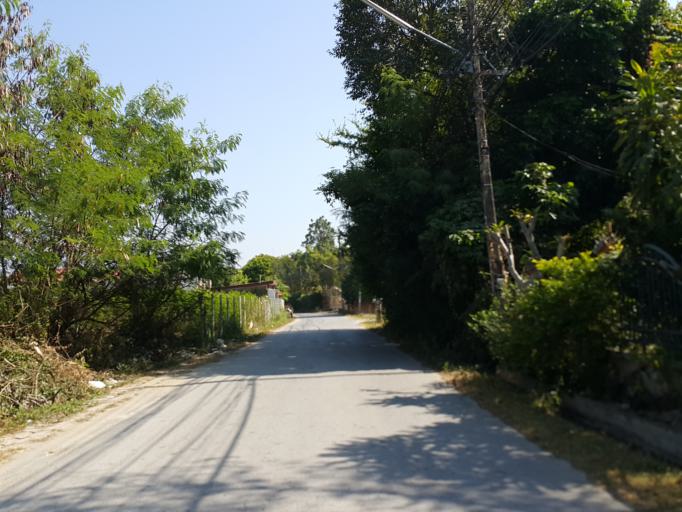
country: TH
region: Chiang Mai
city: Chiang Mai
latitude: 18.8250
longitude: 99.0055
